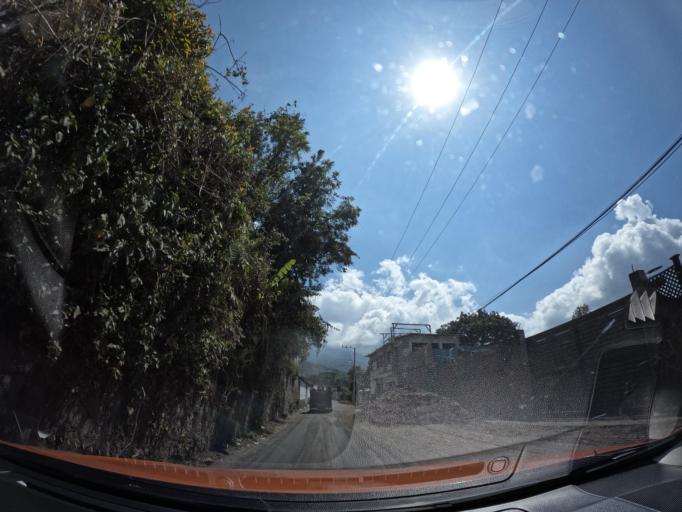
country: GT
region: Solola
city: Santiago Atitlan
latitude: 14.6303
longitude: -91.2321
